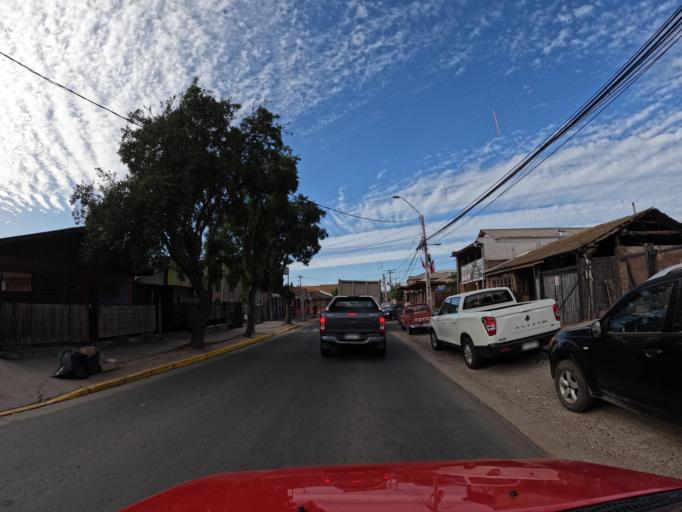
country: CL
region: Valparaiso
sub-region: San Antonio Province
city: San Antonio
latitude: -34.1164
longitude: -71.7268
